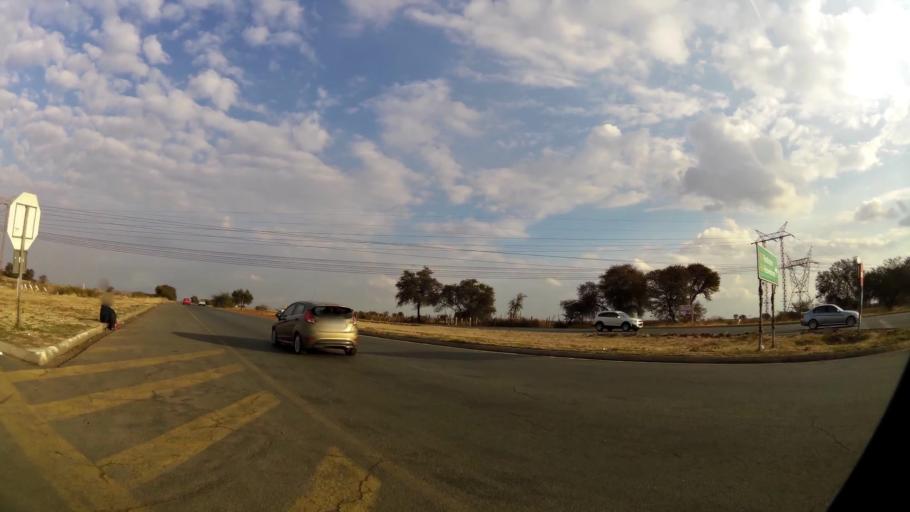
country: ZA
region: Gauteng
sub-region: Sedibeng District Municipality
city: Vereeniging
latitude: -26.6227
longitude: 27.8526
